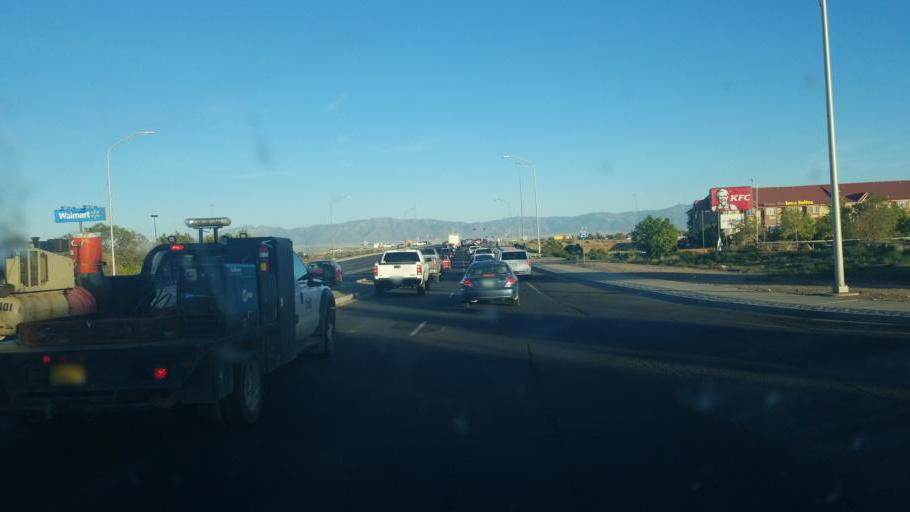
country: US
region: New Mexico
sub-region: Valencia County
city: Los Lunas
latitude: 34.8155
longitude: -106.7652
